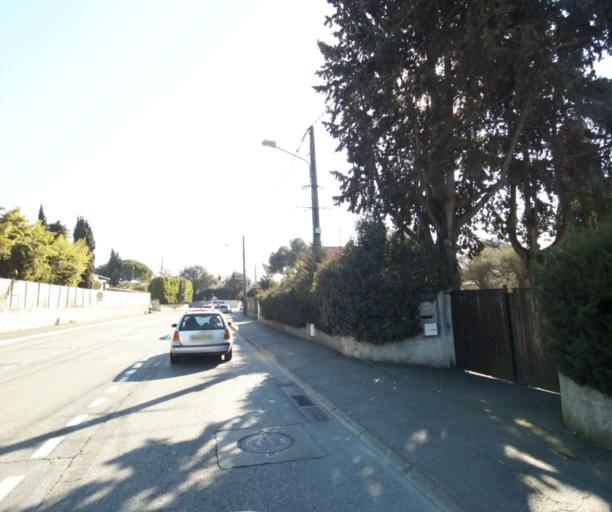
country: FR
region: Provence-Alpes-Cote d'Azur
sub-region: Departement des Alpes-Maritimes
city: Biot
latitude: 43.5978
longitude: 7.1038
